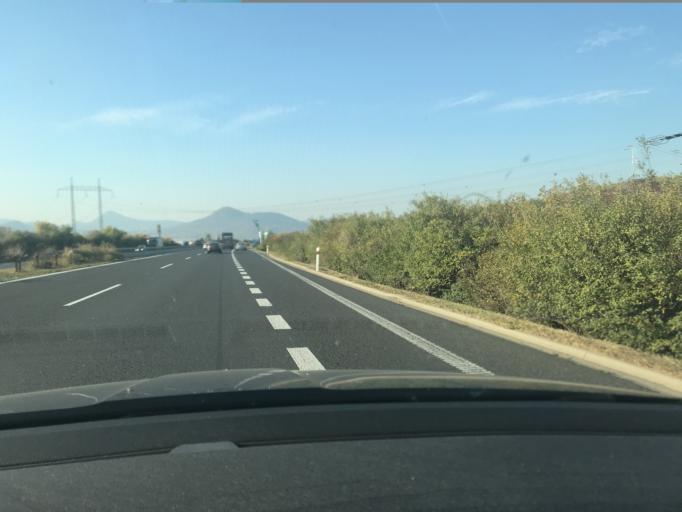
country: CZ
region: Ustecky
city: Lovosice
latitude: 50.4775
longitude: 14.0871
